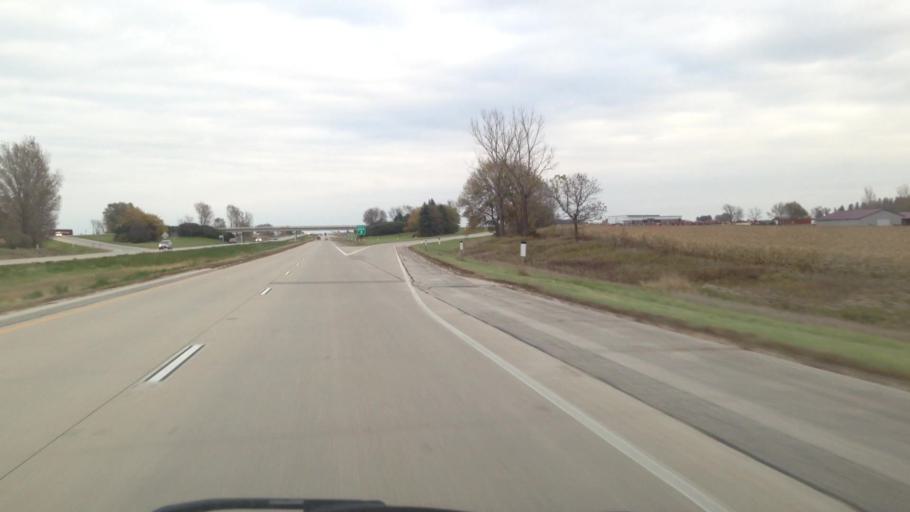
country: US
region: Minnesota
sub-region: Olmsted County
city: Eyota
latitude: 43.9550
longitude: -92.2450
